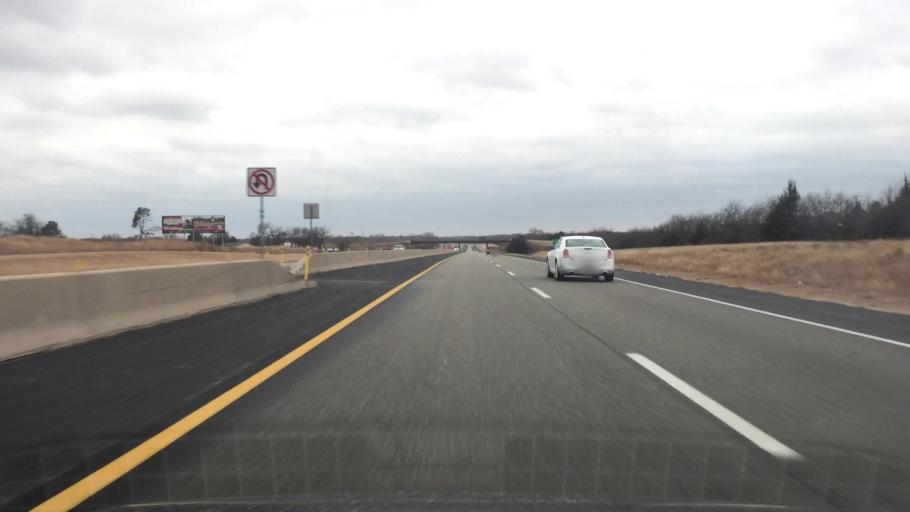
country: US
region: Kansas
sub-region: Butler County
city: Andover
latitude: 37.7038
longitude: -97.1486
